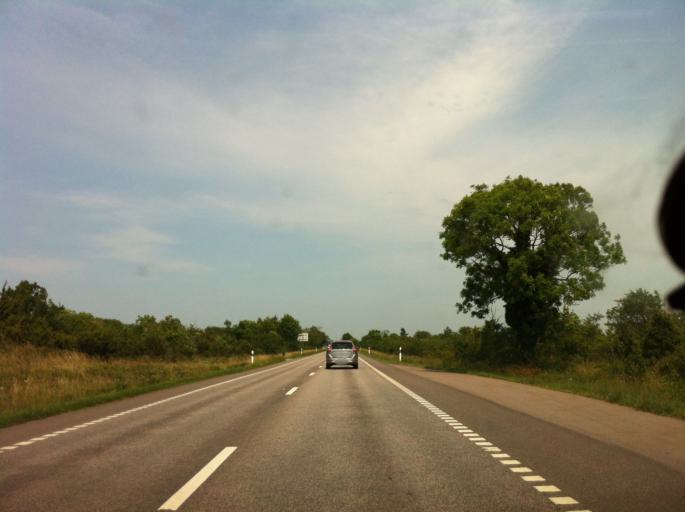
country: SE
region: Kalmar
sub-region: Borgholms Kommun
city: Borgholm
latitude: 56.8079
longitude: 16.5947
